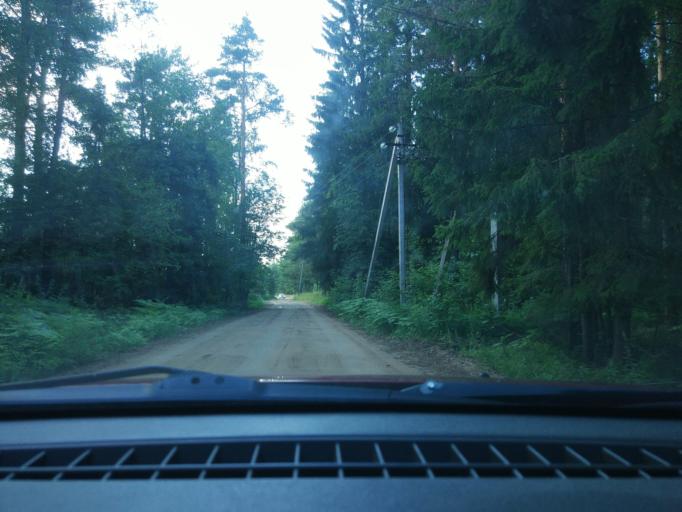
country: RU
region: Leningrad
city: Priozersk
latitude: 60.9321
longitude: 30.0512
